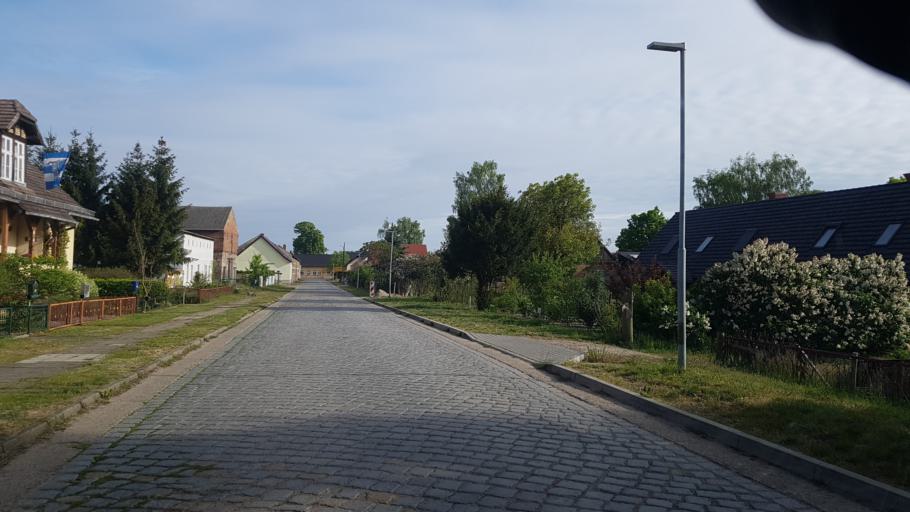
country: DE
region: Brandenburg
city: Baruth
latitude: 52.0485
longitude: 13.4709
